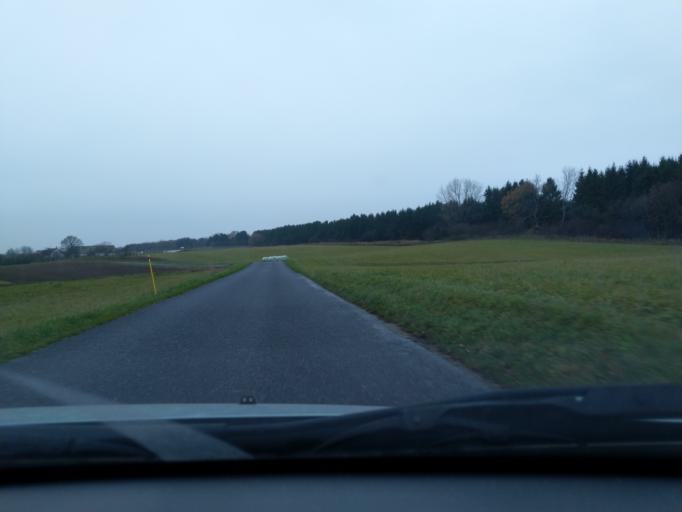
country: DK
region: Zealand
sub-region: Vordingborg Kommune
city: Praesto
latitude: 55.1113
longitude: 12.0887
